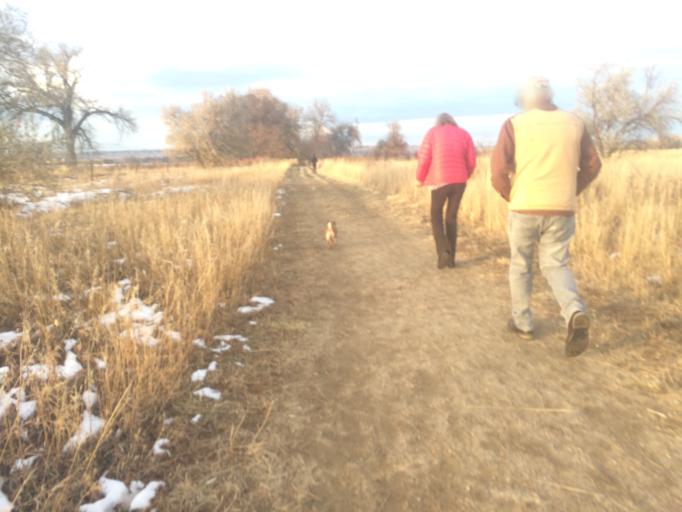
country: US
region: Colorado
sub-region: Boulder County
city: Gunbarrel
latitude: 40.0220
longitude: -105.1546
